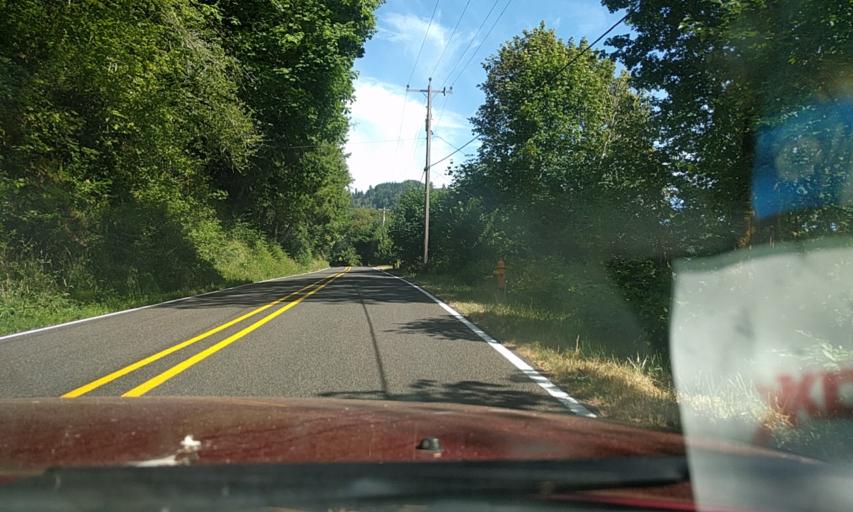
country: US
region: Oregon
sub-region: Lane County
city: Florence
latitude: 44.0377
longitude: -123.8608
